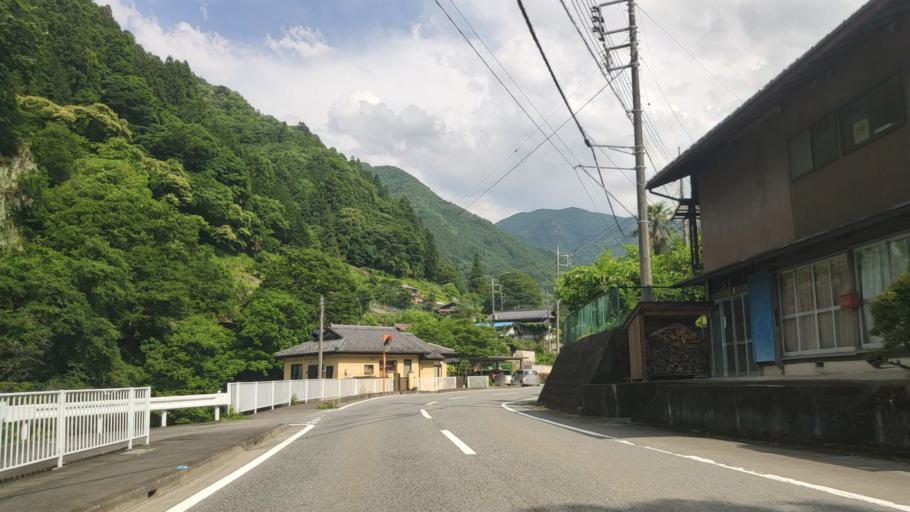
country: JP
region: Gunma
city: Tomioka
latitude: 36.1516
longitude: 138.7300
